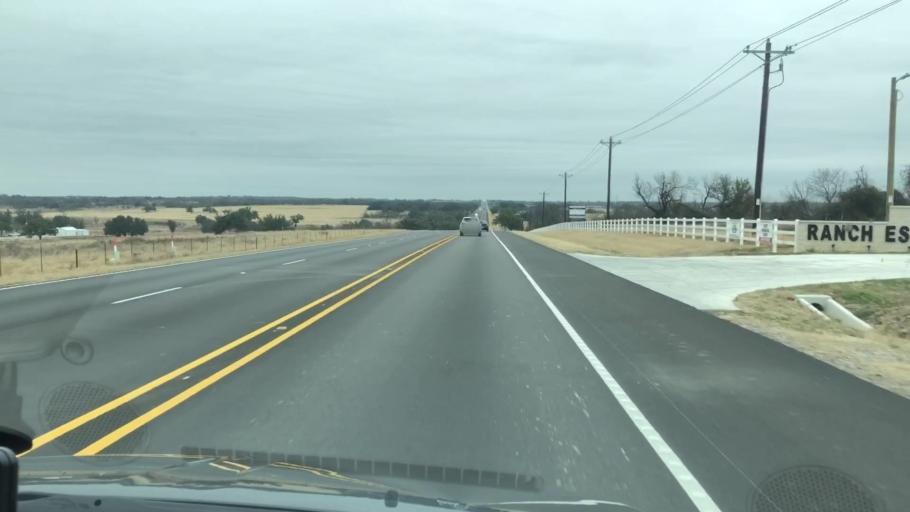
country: US
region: Texas
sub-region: Erath County
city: Stephenville
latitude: 32.2973
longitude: -98.1887
